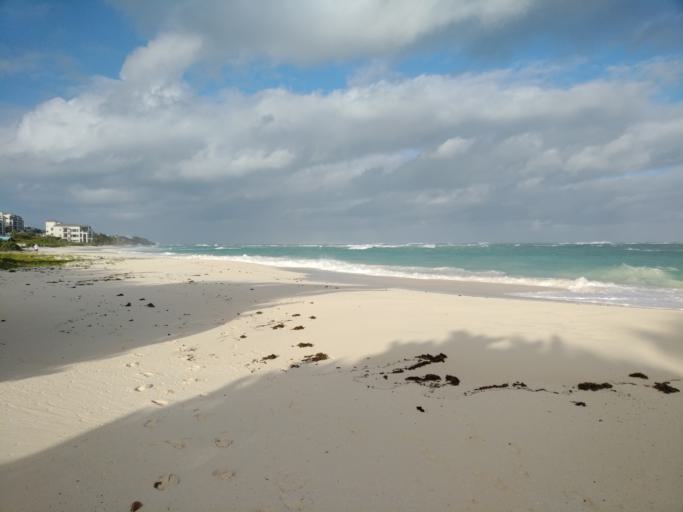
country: AI
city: Island Harbour
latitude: 18.2540
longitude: -63.0327
